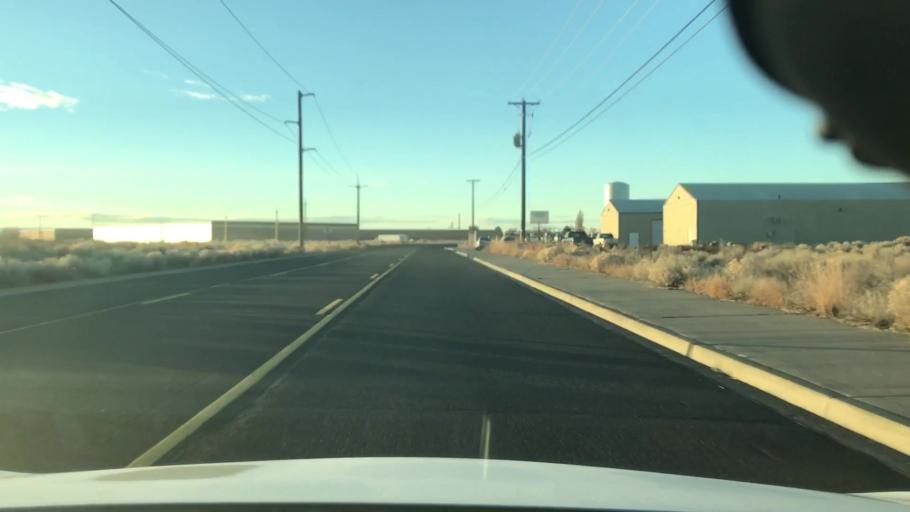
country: US
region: Washington
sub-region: Grant County
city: Moses Lake North
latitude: 47.1772
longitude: -119.3166
